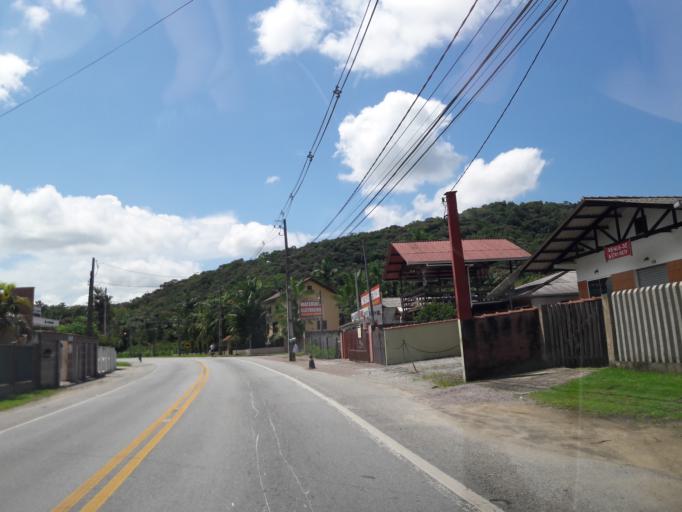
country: BR
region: Parana
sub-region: Antonina
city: Antonina
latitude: -25.4762
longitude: -48.8293
